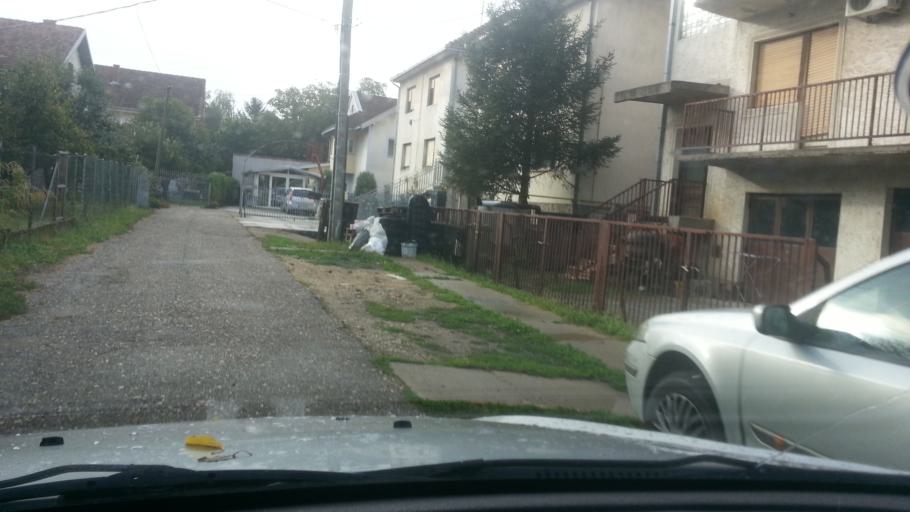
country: RS
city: Novi Banovci
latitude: 44.9467
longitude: 20.2895
